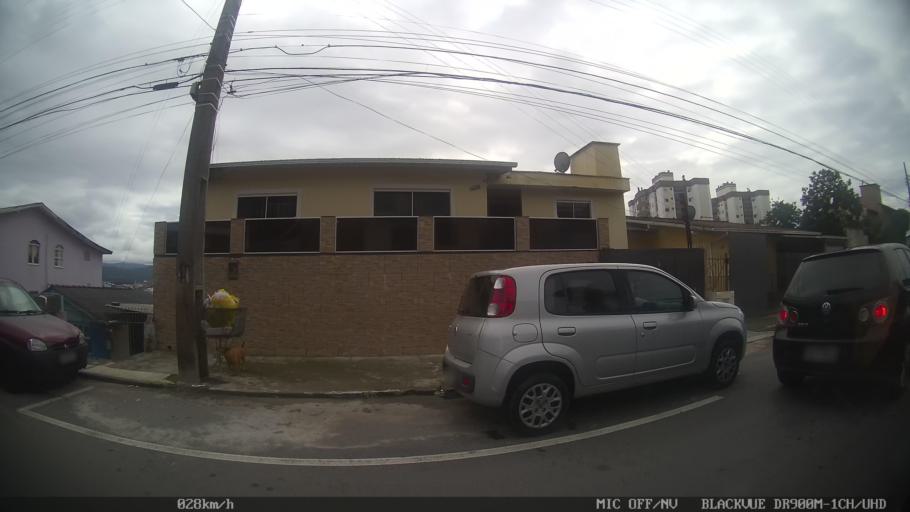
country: BR
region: Santa Catarina
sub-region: Sao Jose
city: Campinas
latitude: -27.5706
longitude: -48.6236
